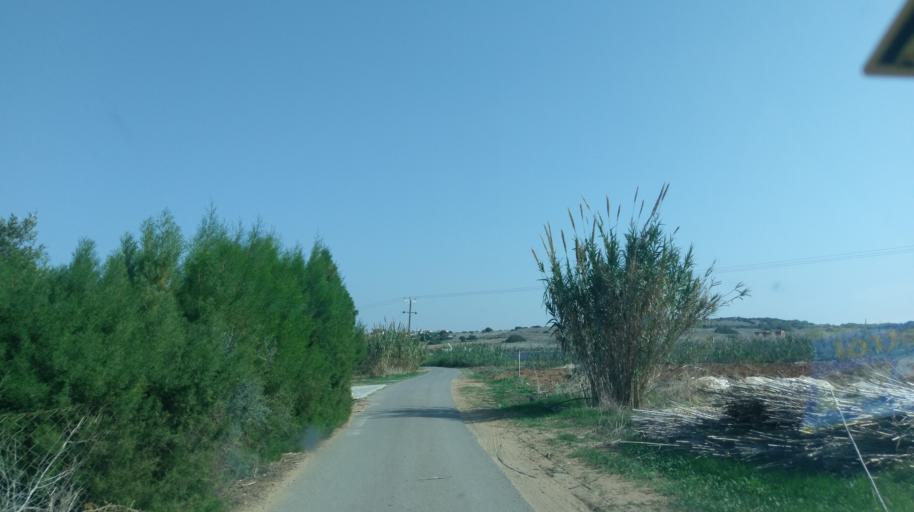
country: CY
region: Lefkosia
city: Morfou
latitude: 35.2954
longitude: 32.9544
